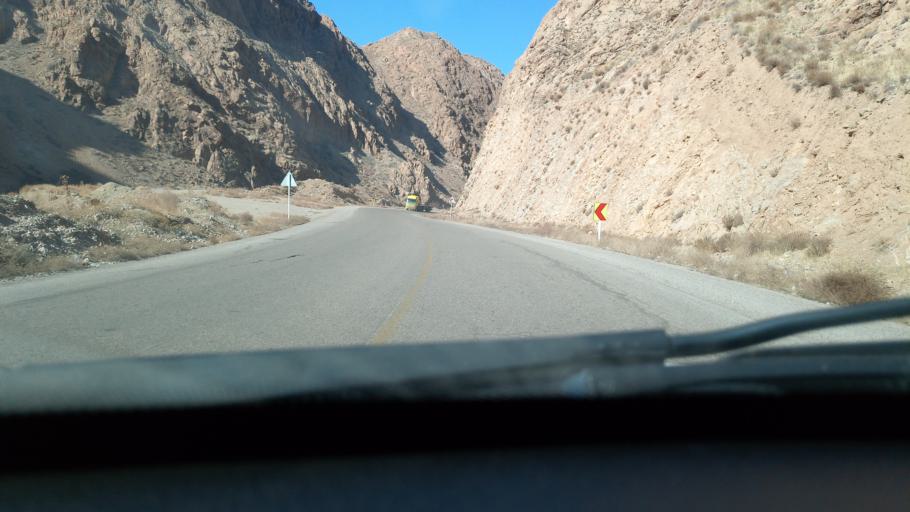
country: IR
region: Khorasan-e Shomali
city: Esfarayen
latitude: 37.1713
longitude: 57.4244
